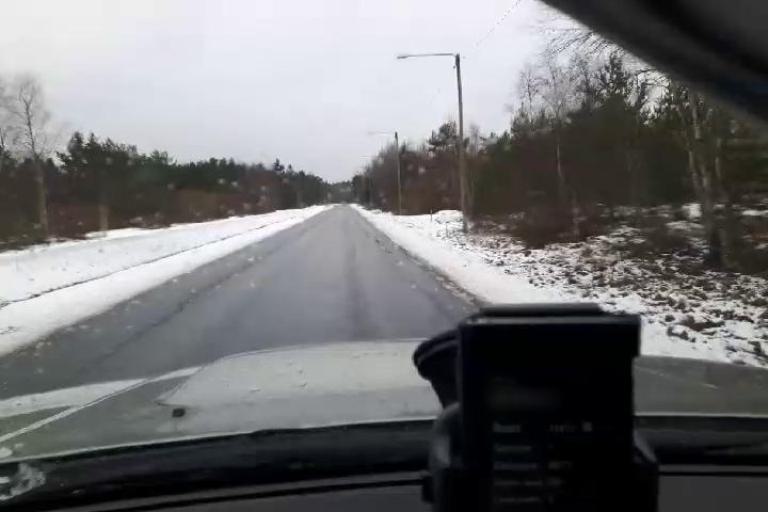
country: EE
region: Harju
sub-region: Harku vald
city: Tabasalu
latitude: 59.4334
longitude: 24.4942
